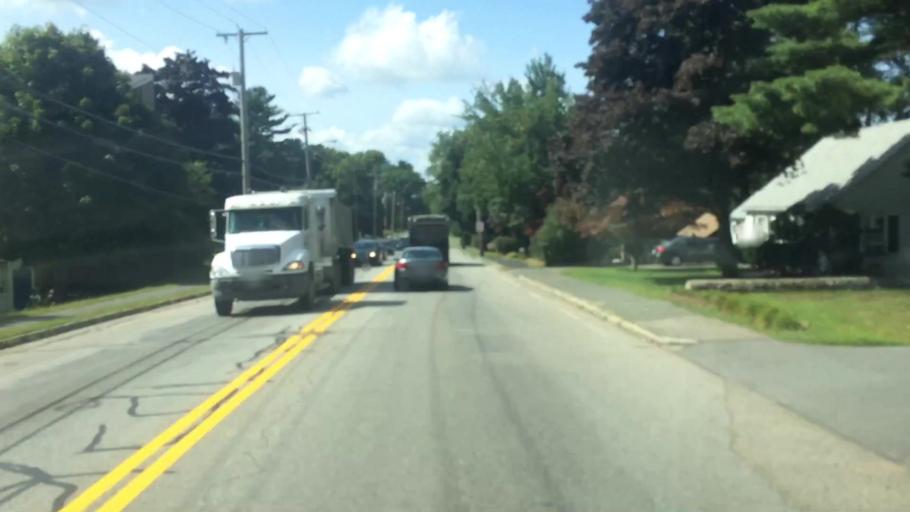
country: US
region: Massachusetts
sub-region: Essex County
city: South Peabody
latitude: 42.5061
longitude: -70.9830
